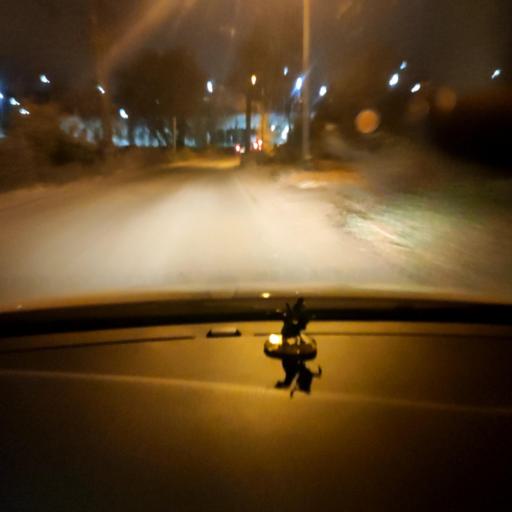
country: RU
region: Tatarstan
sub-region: Gorod Kazan'
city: Kazan
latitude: 55.7288
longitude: 49.1578
